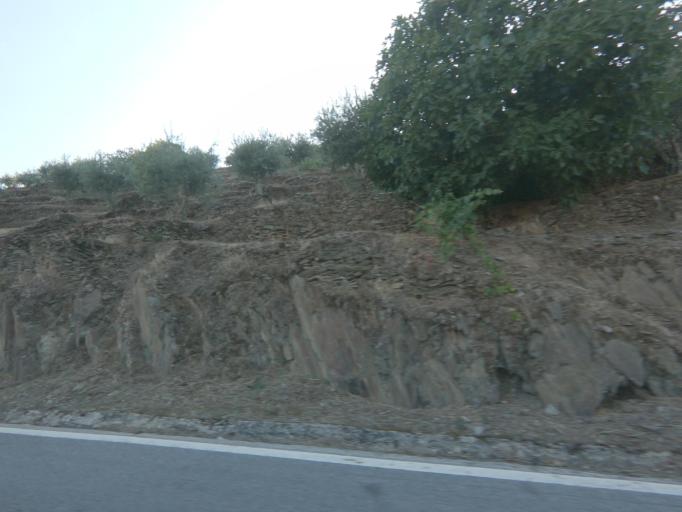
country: PT
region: Viseu
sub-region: Tabuaco
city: Tabuaco
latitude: 41.1356
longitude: -7.5677
